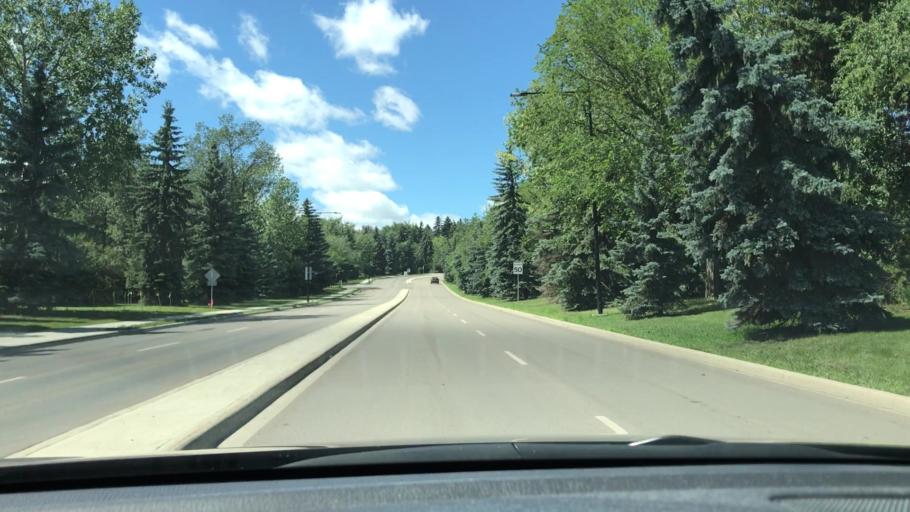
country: CA
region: Alberta
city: Edmonton
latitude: 53.5128
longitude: -113.5519
